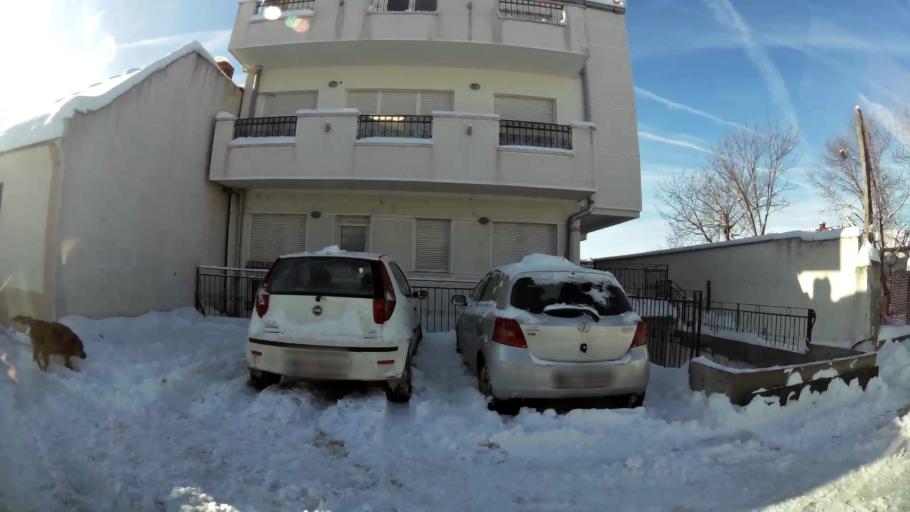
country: RS
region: Central Serbia
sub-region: Belgrade
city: Palilula
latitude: 44.7903
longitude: 20.5122
